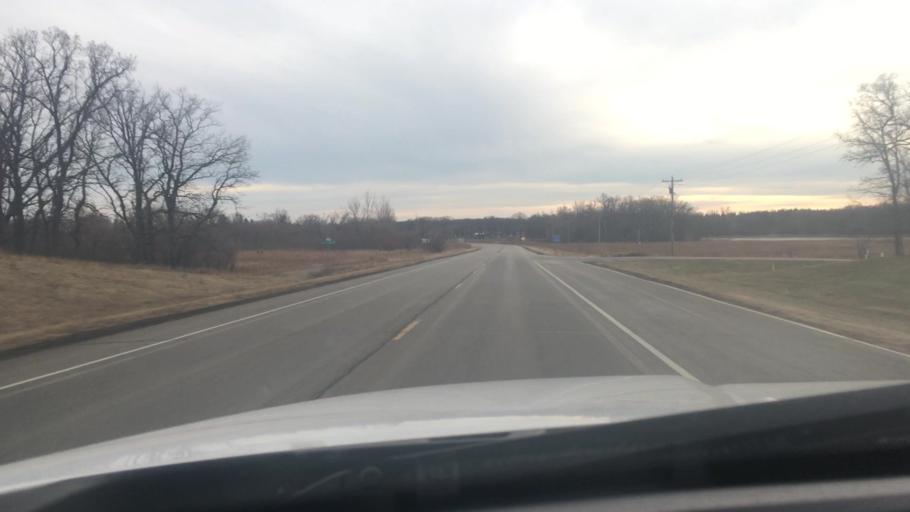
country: US
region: Minnesota
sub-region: Otter Tail County
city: Perham
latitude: 46.2982
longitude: -95.7181
